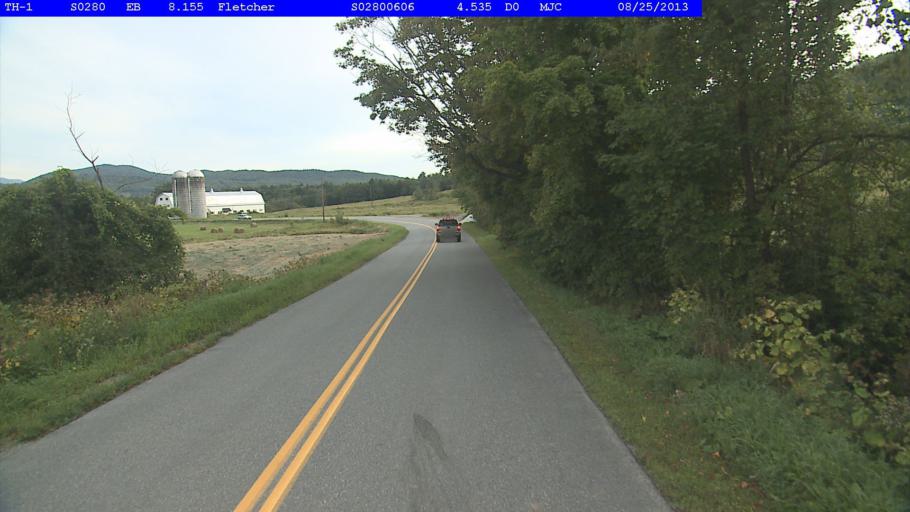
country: US
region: Vermont
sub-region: Chittenden County
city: Jericho
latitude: 44.6667
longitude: -72.8896
